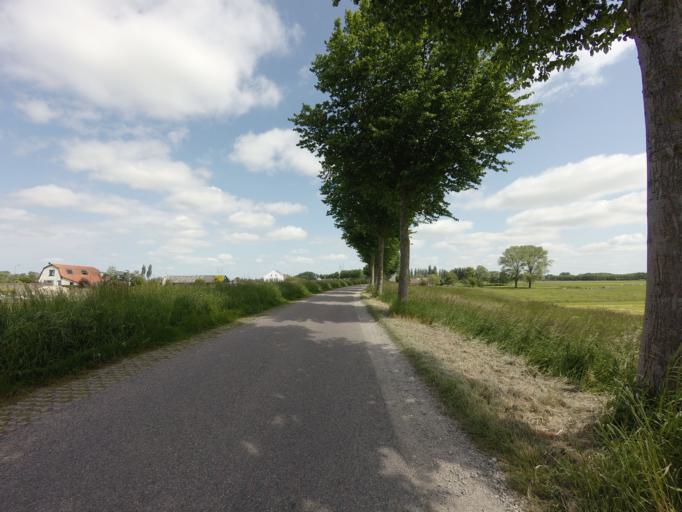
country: NL
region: North Holland
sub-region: Gemeente Beemster
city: Halfweg
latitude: 52.5611
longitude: 4.8604
